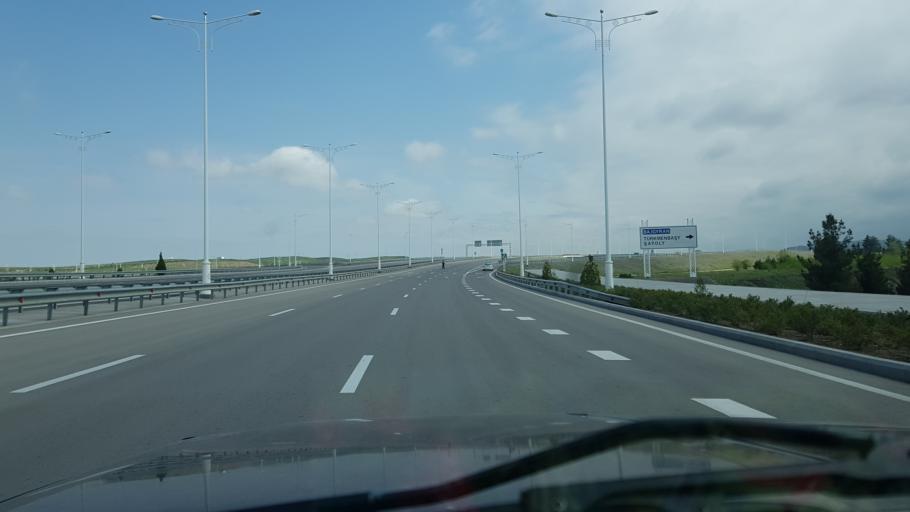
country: TM
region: Ahal
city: Ashgabat
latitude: 37.8631
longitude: 58.3701
